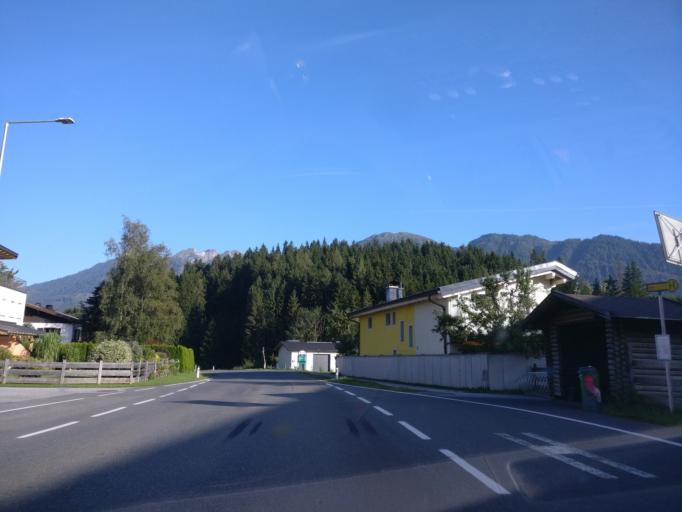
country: AT
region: Salzburg
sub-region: Politischer Bezirk Sankt Johann im Pongau
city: Goldegg
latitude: 47.3233
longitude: 13.0851
